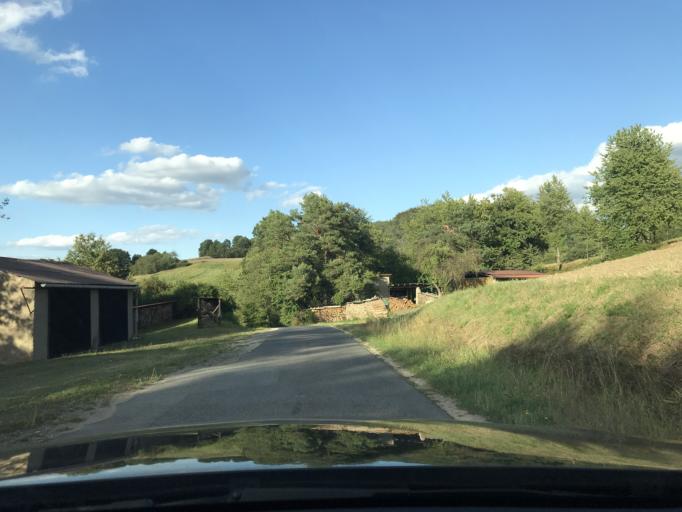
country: DE
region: Bavaria
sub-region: Regierungsbezirk Unterfranken
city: Breitbrunn
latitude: 50.0305
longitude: 10.6872
